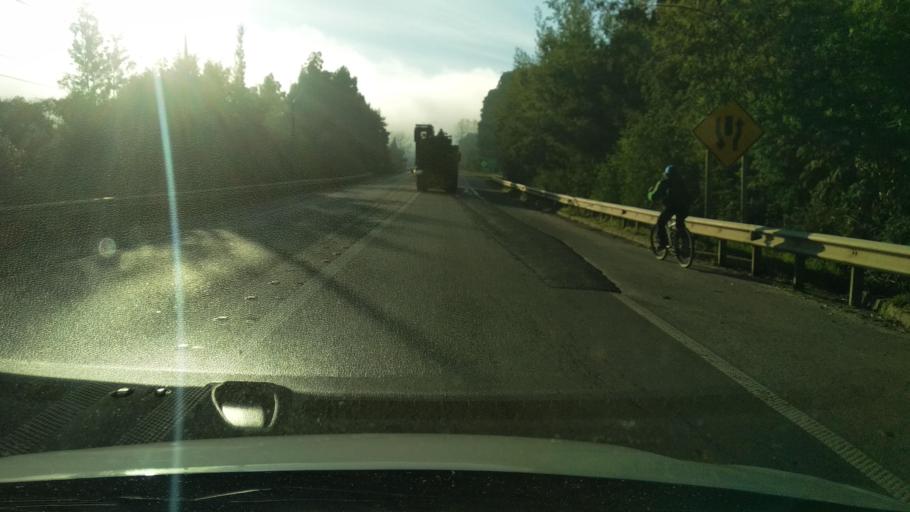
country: CL
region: Los Lagos
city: Las Animas
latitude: -39.7761
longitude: -73.2178
